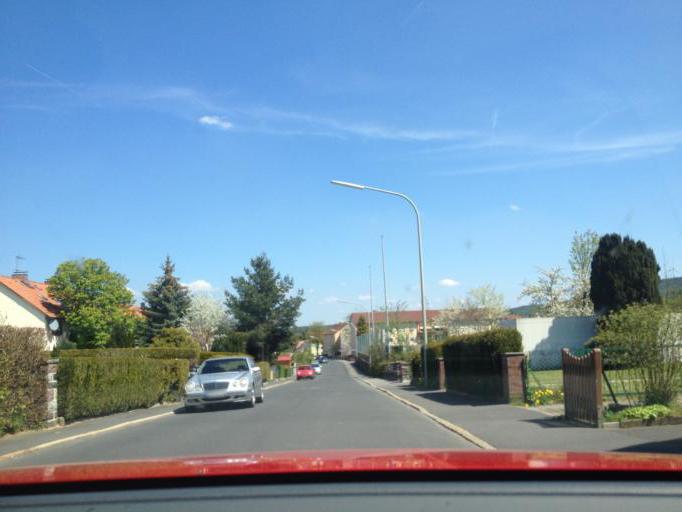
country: DE
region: Bavaria
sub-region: Upper Franconia
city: Arzberg
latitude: 50.0558
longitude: 12.1756
